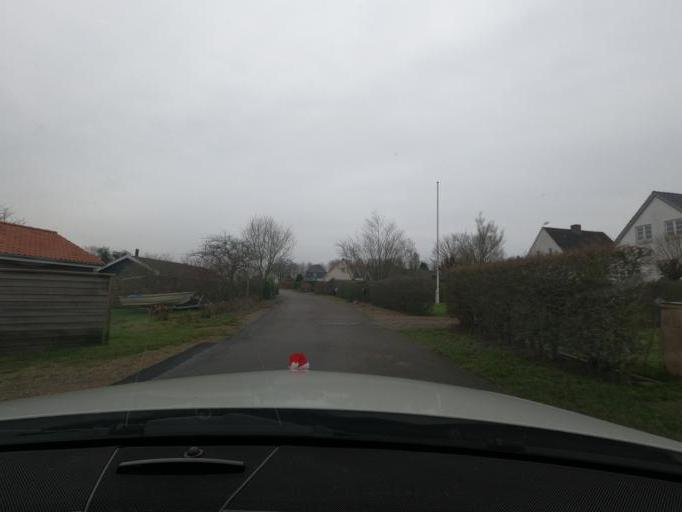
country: DK
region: South Denmark
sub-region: Haderslev Kommune
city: Starup
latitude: 55.1932
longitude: 9.5800
